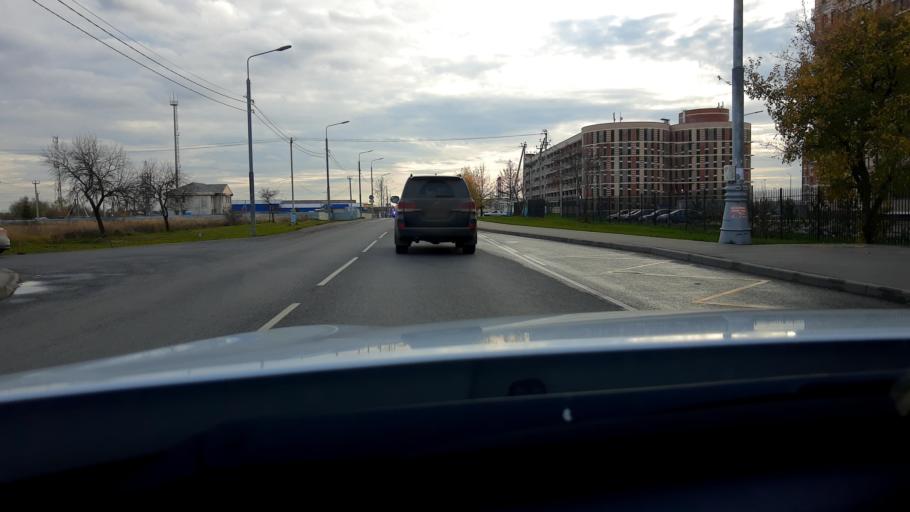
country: RU
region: Moskovskaya
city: Kokoshkino
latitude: 55.5442
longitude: 37.1553
